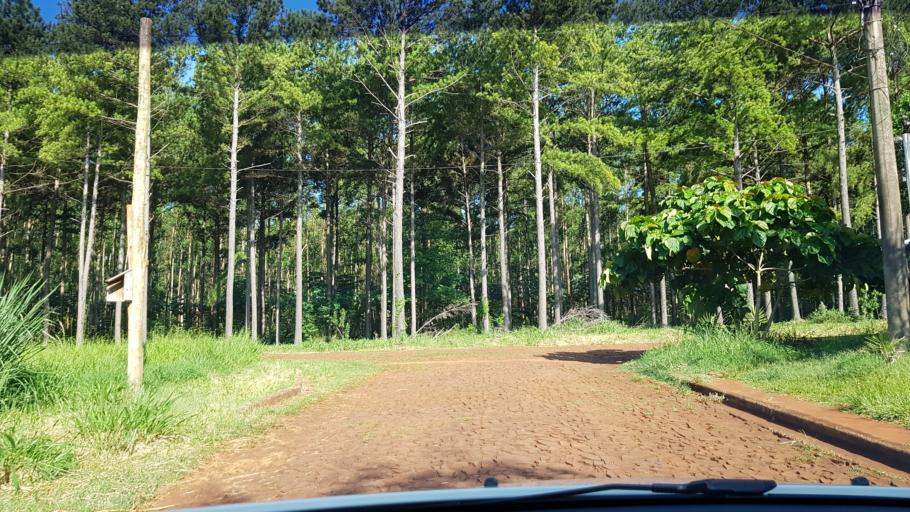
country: AR
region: Misiones
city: Puerto Libertad
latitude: -25.9143
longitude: -54.5778
